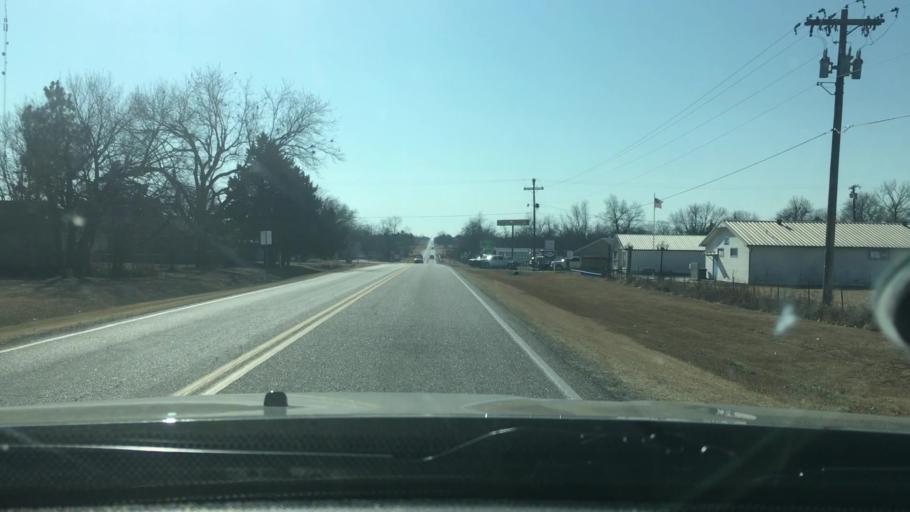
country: US
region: Oklahoma
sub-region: Garvin County
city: Stratford
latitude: 34.7985
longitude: -96.9677
